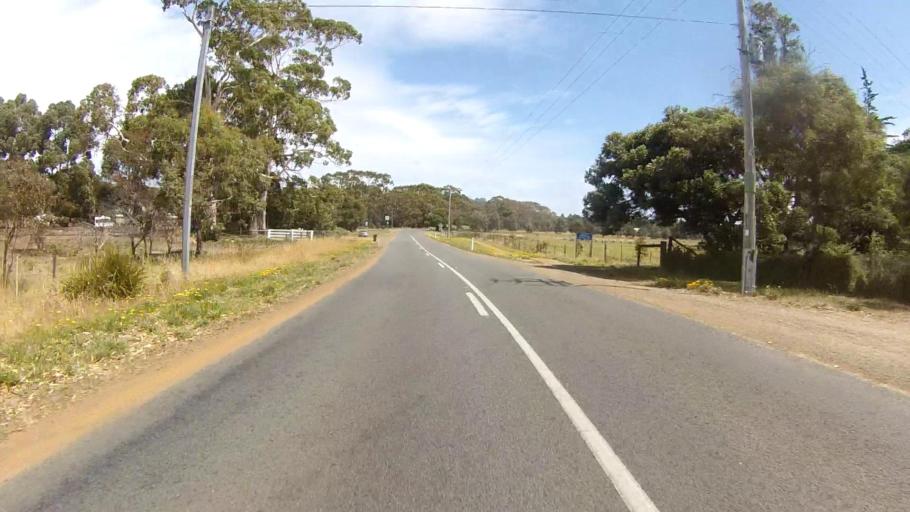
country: AU
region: Tasmania
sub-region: Kingborough
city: Blackmans Bay
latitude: -43.0284
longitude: 147.4305
